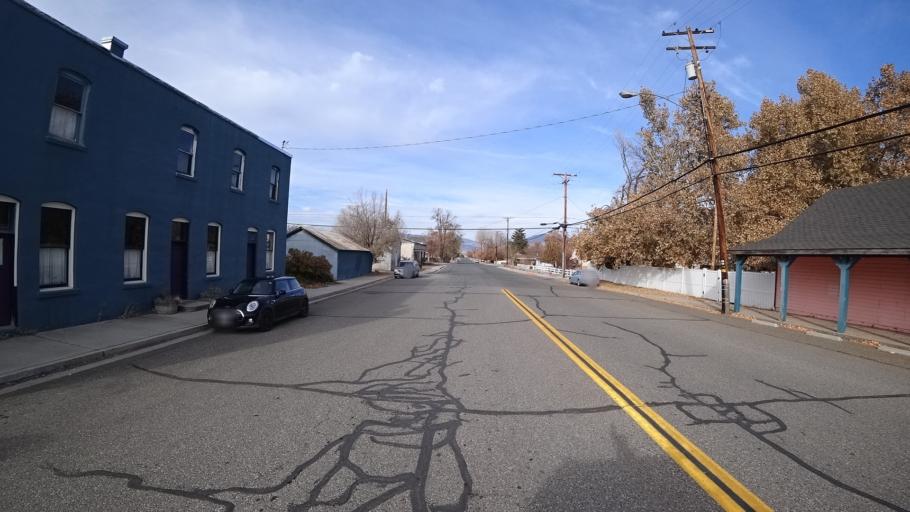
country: US
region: California
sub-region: Siskiyou County
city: Montague
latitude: 41.7283
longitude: -122.5278
